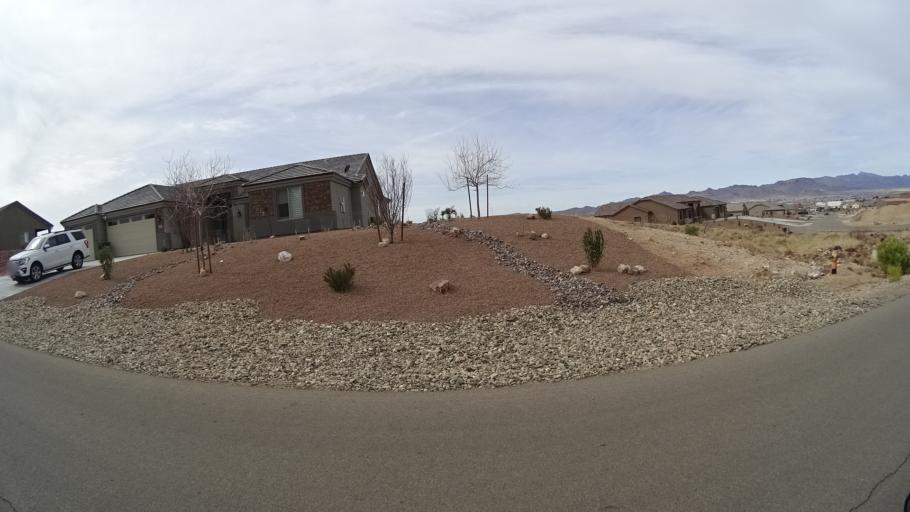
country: US
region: Arizona
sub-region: Mohave County
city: Kingman
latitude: 35.1856
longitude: -113.9763
